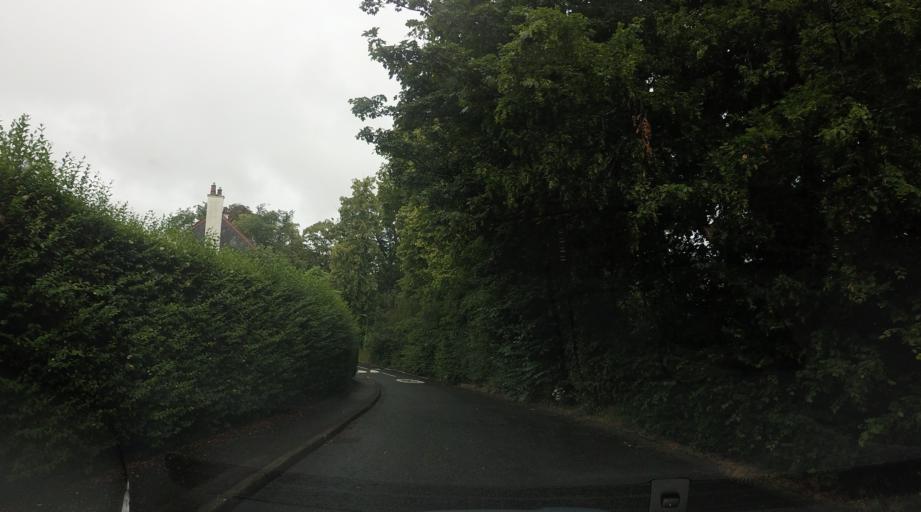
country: GB
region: Scotland
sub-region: West Lothian
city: Broxburn
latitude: 55.9291
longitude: -3.5003
